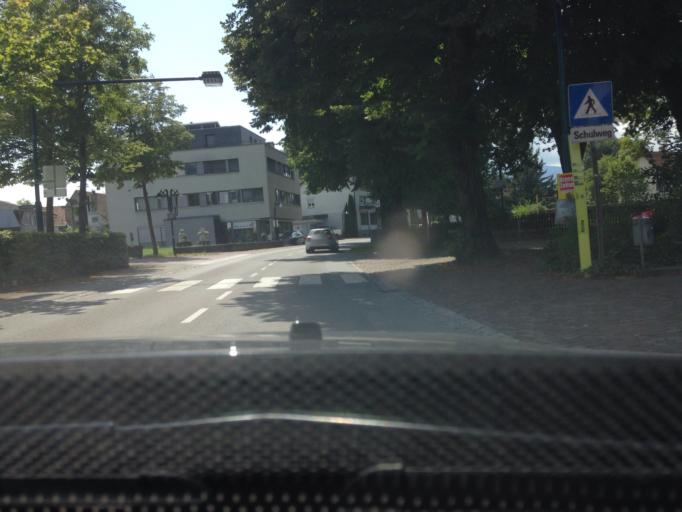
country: AT
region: Vorarlberg
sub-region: Politischer Bezirk Feldkirch
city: Altach
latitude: 47.3542
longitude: 9.6510
